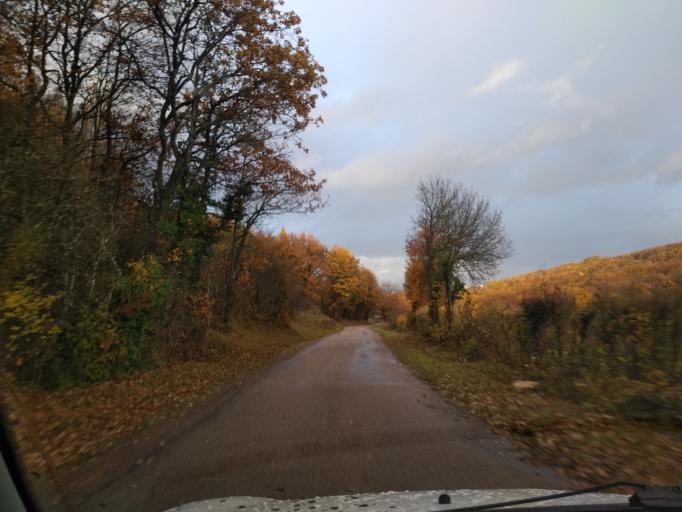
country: FR
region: Bourgogne
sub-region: Departement de Saone-et-Loire
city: Rully
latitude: 46.8810
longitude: 4.7134
